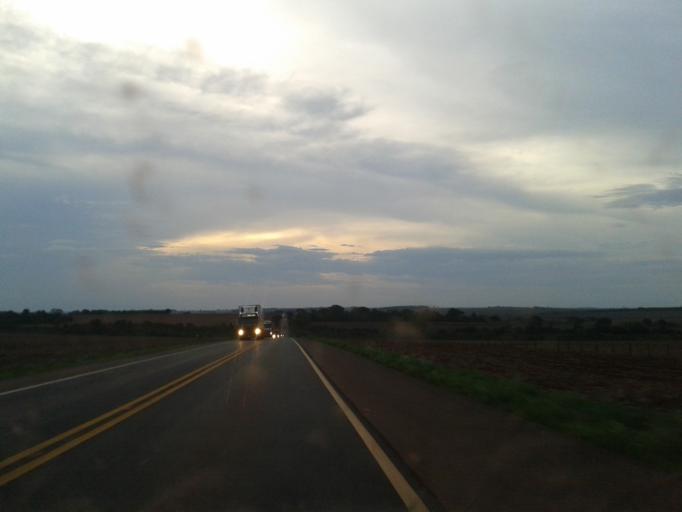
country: BR
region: Goias
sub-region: Santa Helena De Goias
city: Santa Helena de Goias
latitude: -17.8851
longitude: -50.6850
